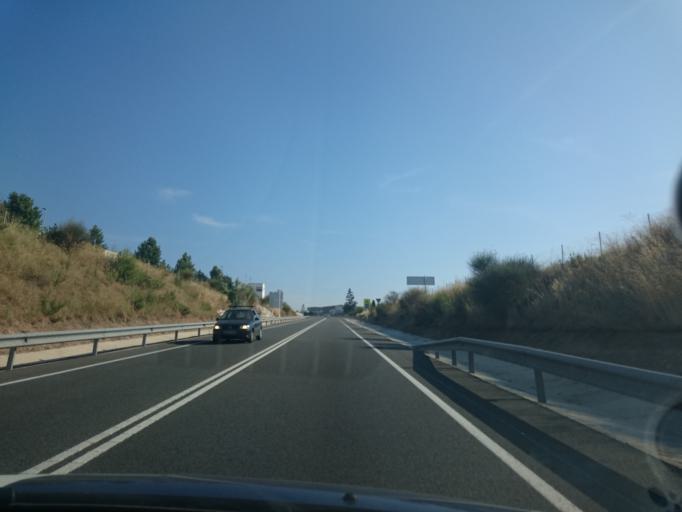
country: ES
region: Catalonia
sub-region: Provincia de Barcelona
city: La Granada
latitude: 41.3765
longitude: 1.7123
